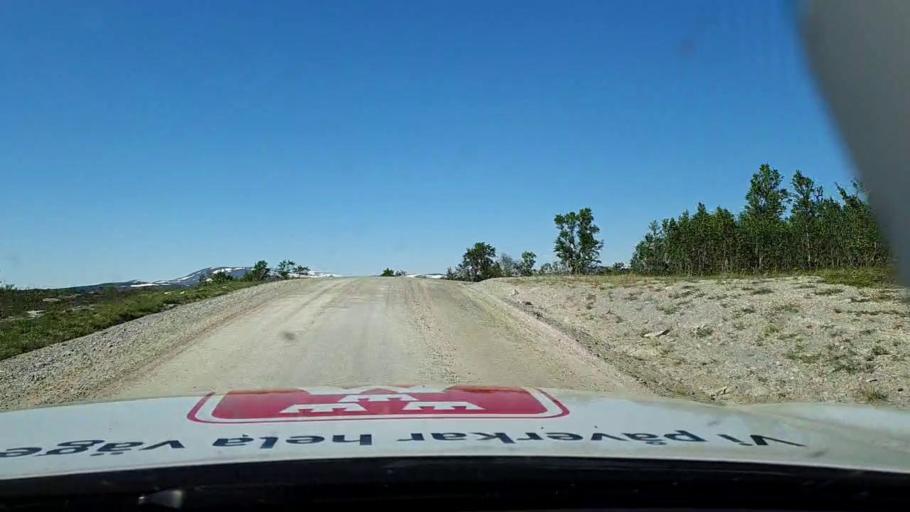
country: SE
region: Jaemtland
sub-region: Are Kommun
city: Are
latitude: 62.6544
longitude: 12.6636
